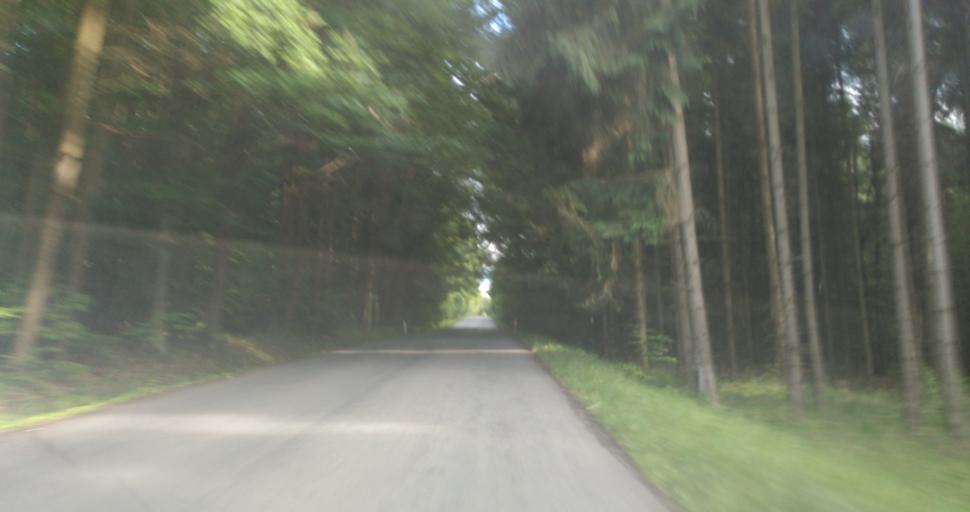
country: CZ
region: Central Bohemia
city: Hudlice
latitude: 49.9624
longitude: 13.9173
